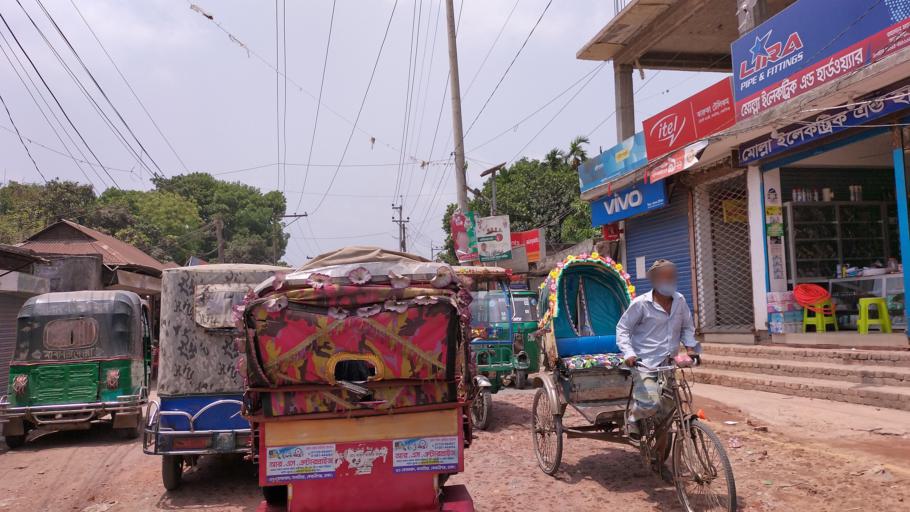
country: BD
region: Dhaka
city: Azimpur
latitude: 23.7329
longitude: 90.2731
